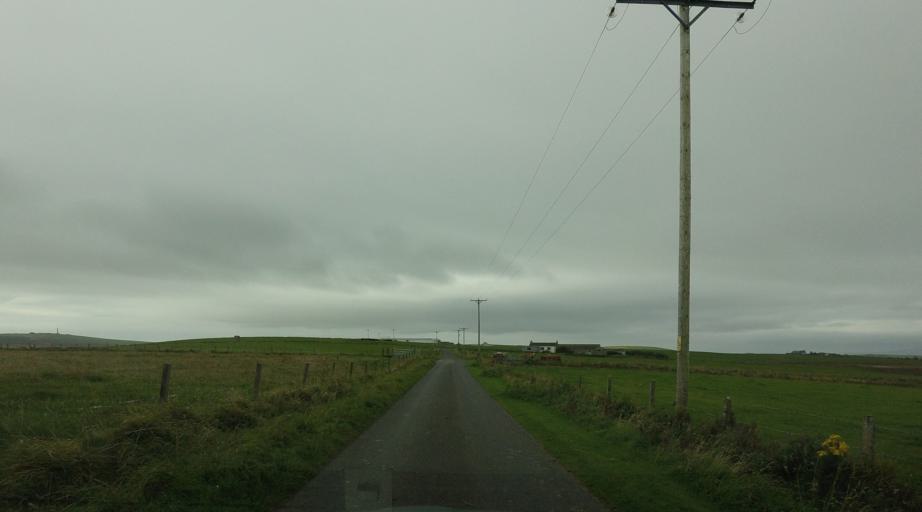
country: GB
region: Scotland
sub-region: Orkney Islands
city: Orkney
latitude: 58.8049
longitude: -2.9389
